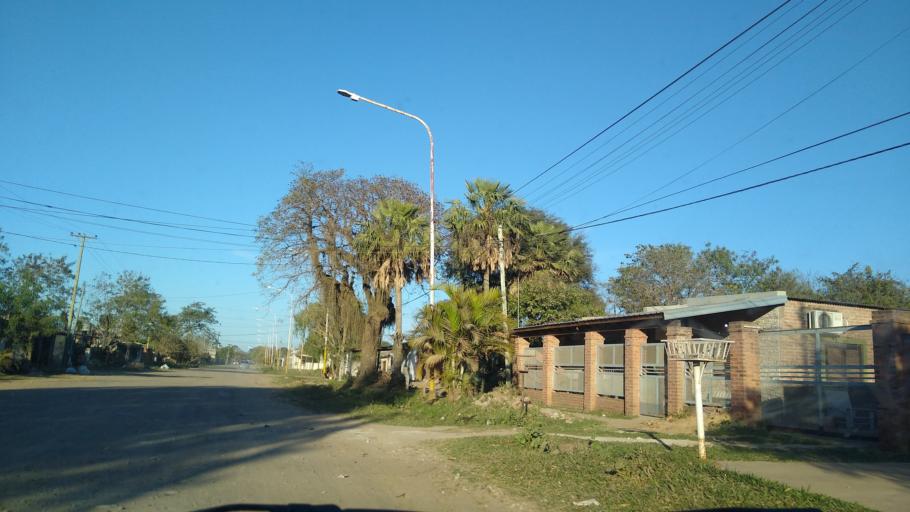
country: AR
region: Chaco
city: Barranqueras
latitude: -27.4777
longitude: -58.9449
